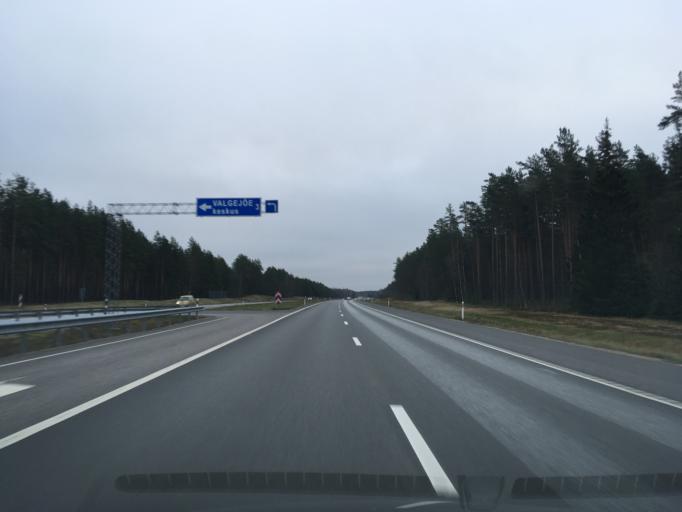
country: EE
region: Harju
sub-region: Loksa linn
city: Loksa
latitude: 59.4639
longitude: 25.7451
